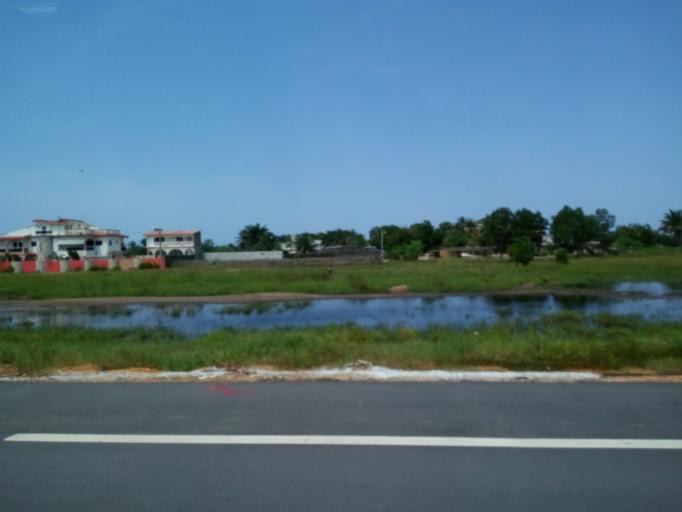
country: CI
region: Sud-Comoe
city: Grand-Bassam
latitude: 5.2244
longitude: -3.7310
